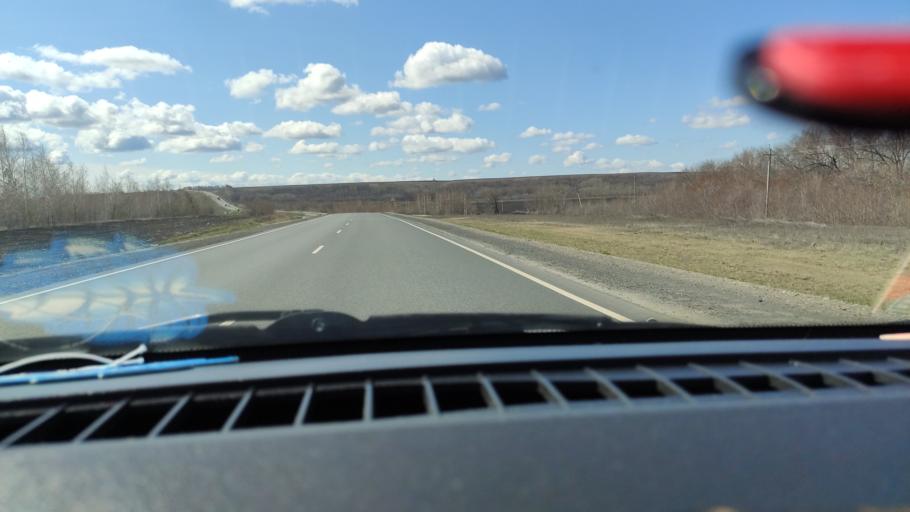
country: RU
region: Samara
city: Syzran'
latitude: 52.9723
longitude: 48.3085
